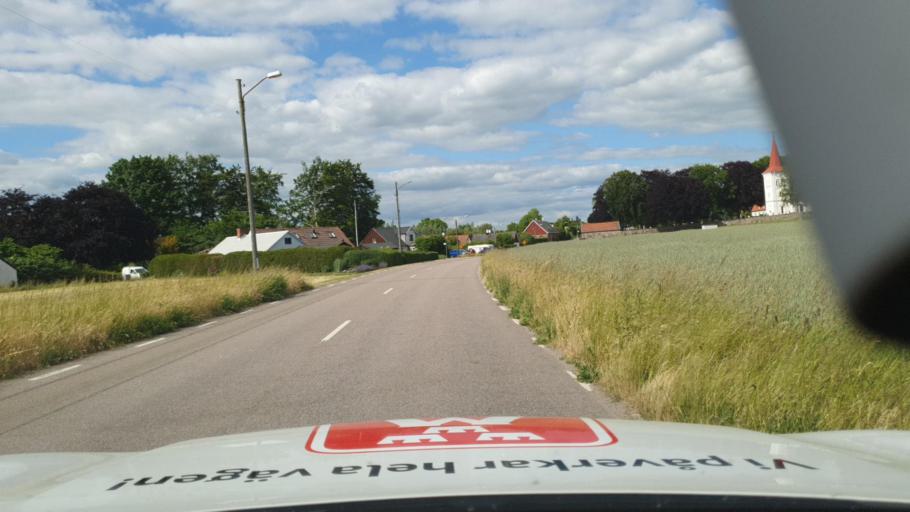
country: SE
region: Skane
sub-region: Ystads Kommun
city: Kopingebro
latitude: 55.4687
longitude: 13.9446
